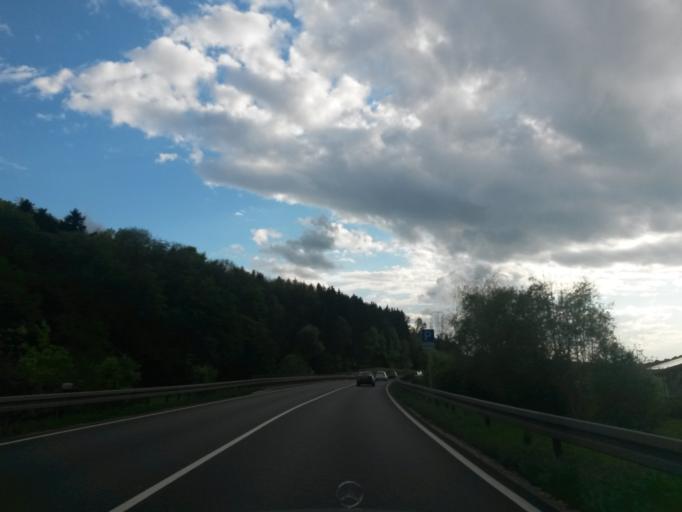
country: DE
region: Baden-Wuerttemberg
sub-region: Regierungsbezirk Stuttgart
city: Iggingen
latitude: 48.8128
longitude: 9.8723
